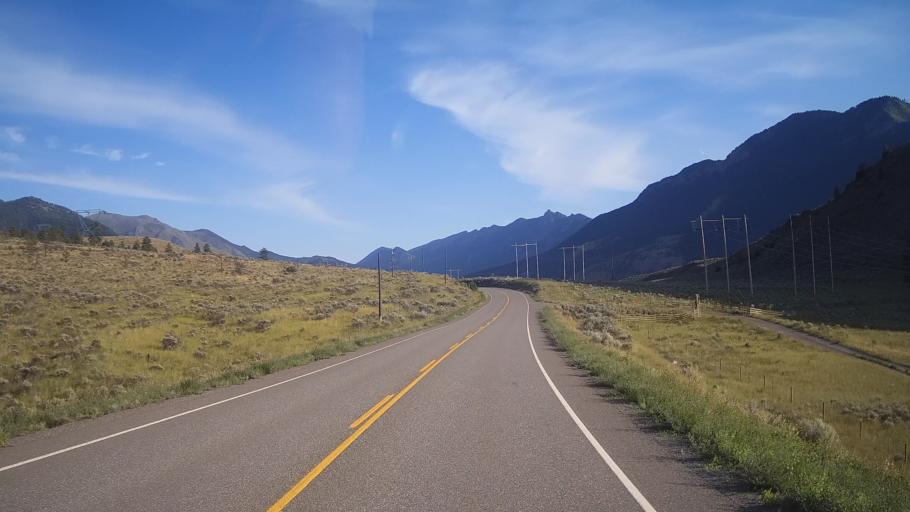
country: CA
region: British Columbia
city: Lillooet
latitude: 50.8233
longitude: -121.8565
